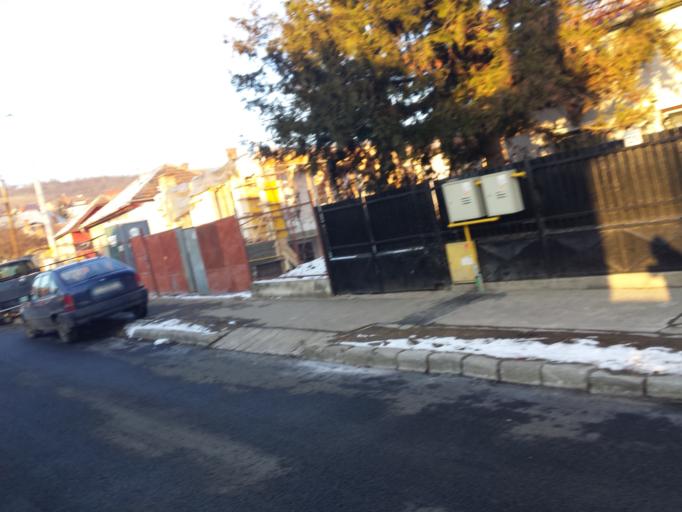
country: RO
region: Cluj
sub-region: Municipiul Cluj-Napoca
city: Cluj-Napoca
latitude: 46.7899
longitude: 23.5870
